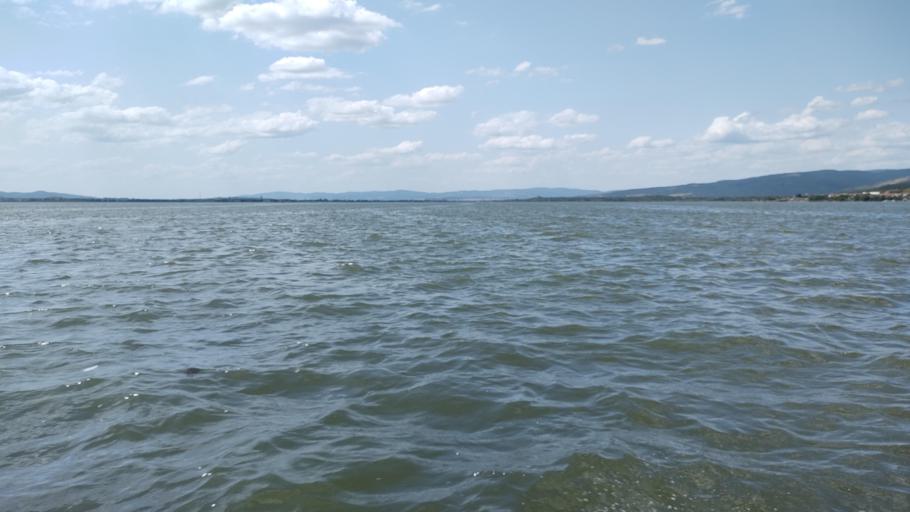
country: RO
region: Caras-Severin
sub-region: Comuna Pescari
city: Coronini
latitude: 44.6720
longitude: 21.6770
